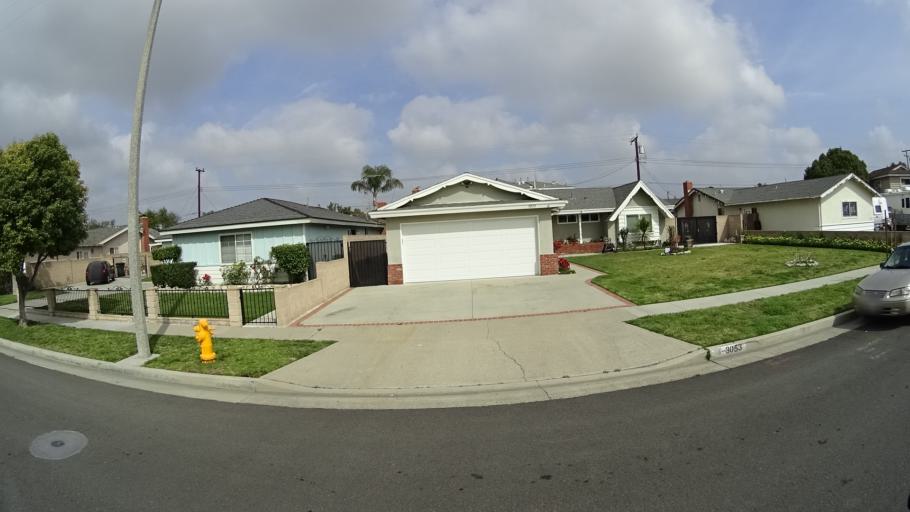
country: US
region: California
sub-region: Orange County
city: Stanton
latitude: 33.8192
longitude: -117.9963
